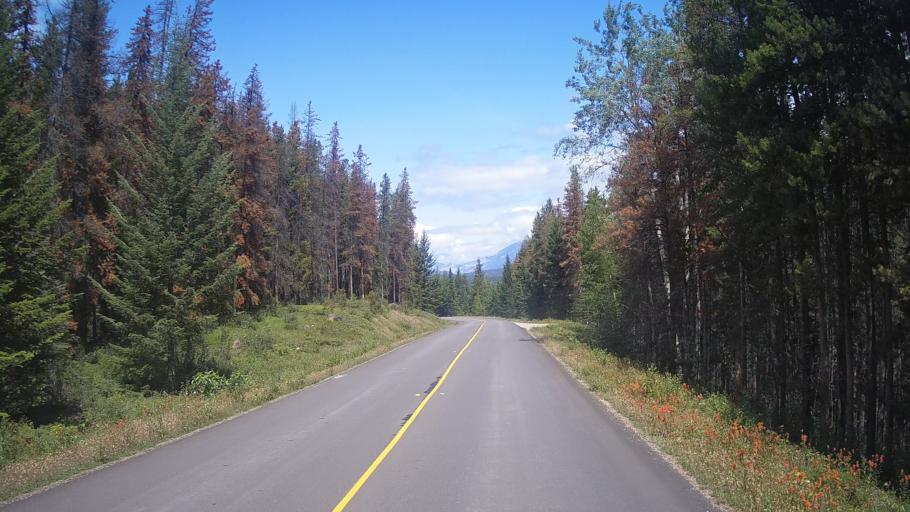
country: CA
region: Alberta
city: Jasper Park Lodge
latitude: 52.7844
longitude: -118.0326
